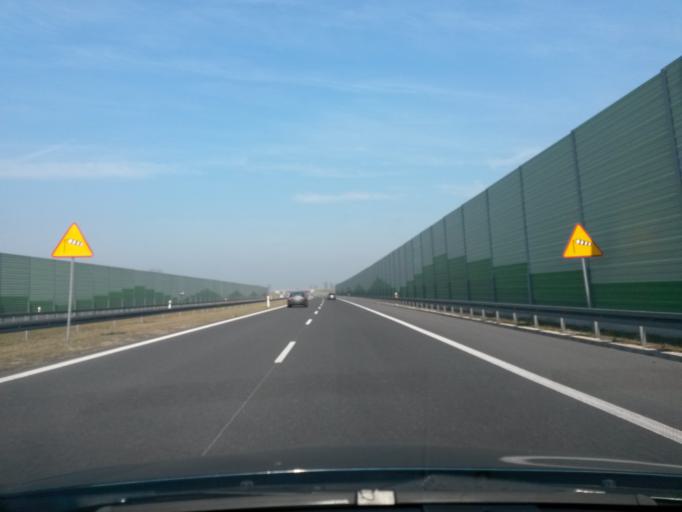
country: PL
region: Lodz Voivodeship
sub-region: Powiat leczycki
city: Piatek
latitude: 52.1184
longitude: 19.5024
